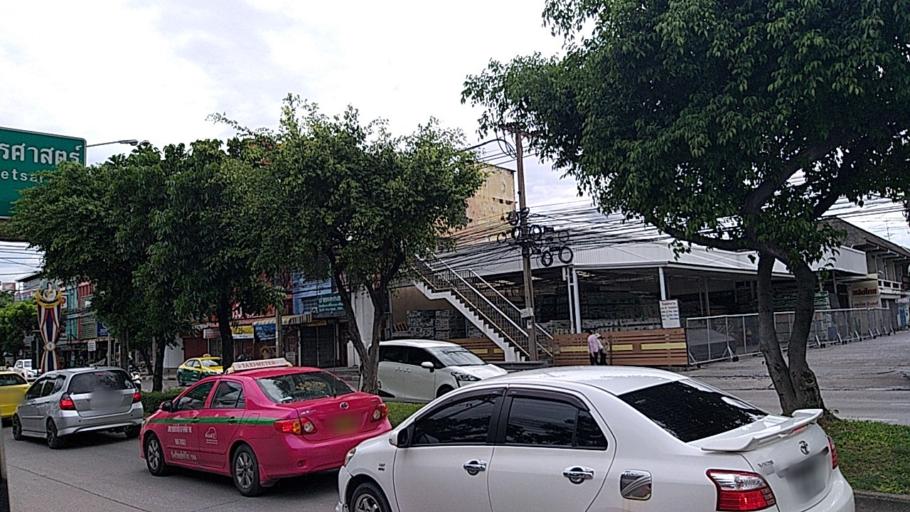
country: TH
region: Bangkok
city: Khan Na Yao
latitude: 13.8128
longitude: 100.6514
